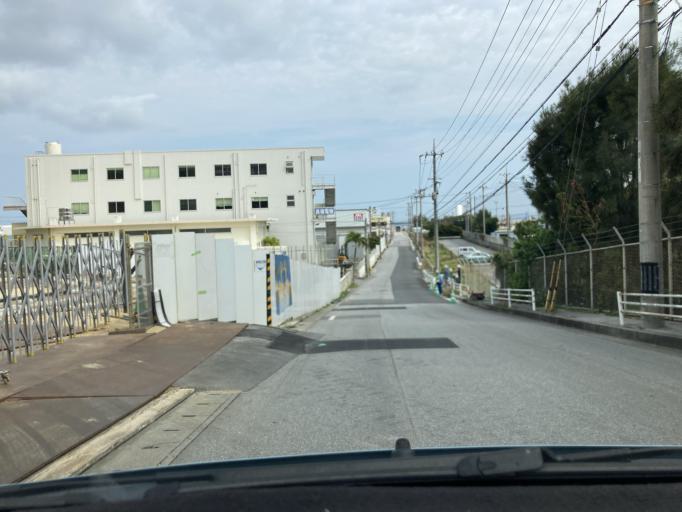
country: JP
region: Okinawa
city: Ginowan
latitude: 26.2700
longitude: 127.7153
